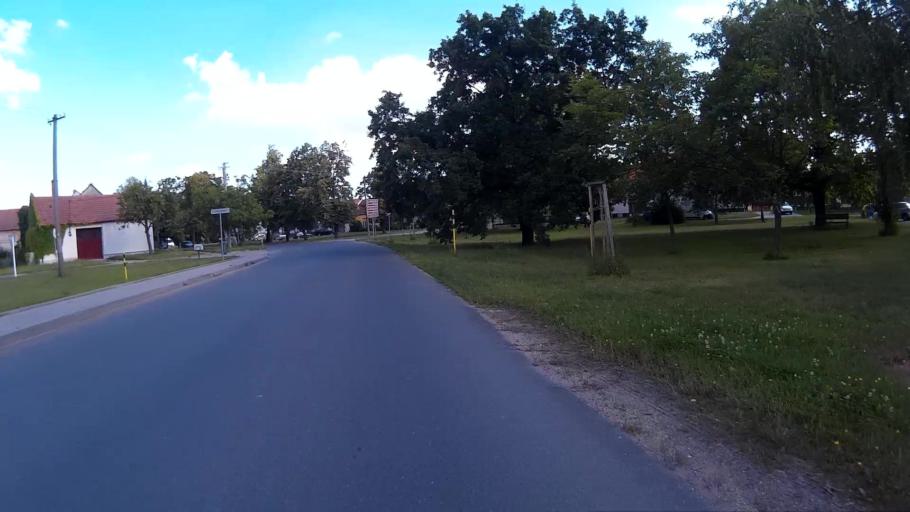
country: CZ
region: South Moravian
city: Tesany
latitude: 49.0437
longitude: 16.7658
